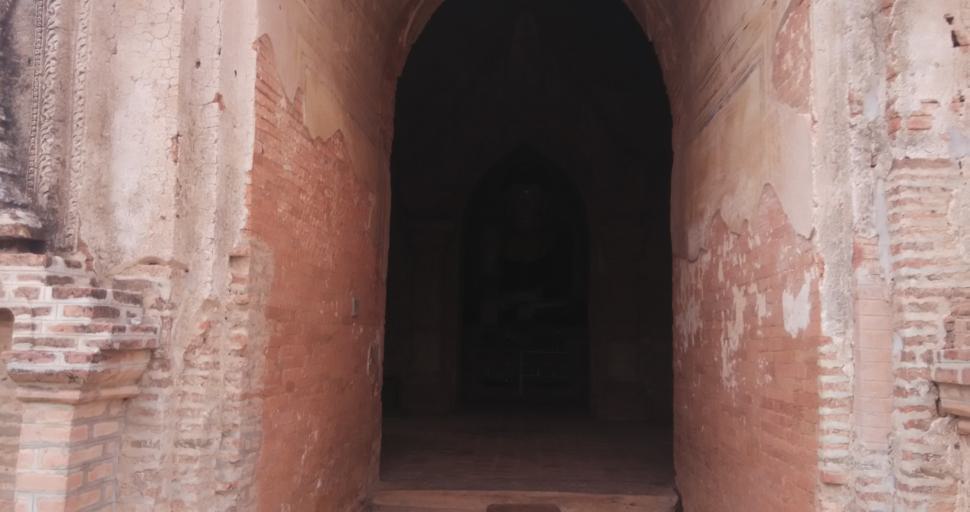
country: MM
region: Magway
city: Pakokku
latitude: 21.1659
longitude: 94.8837
